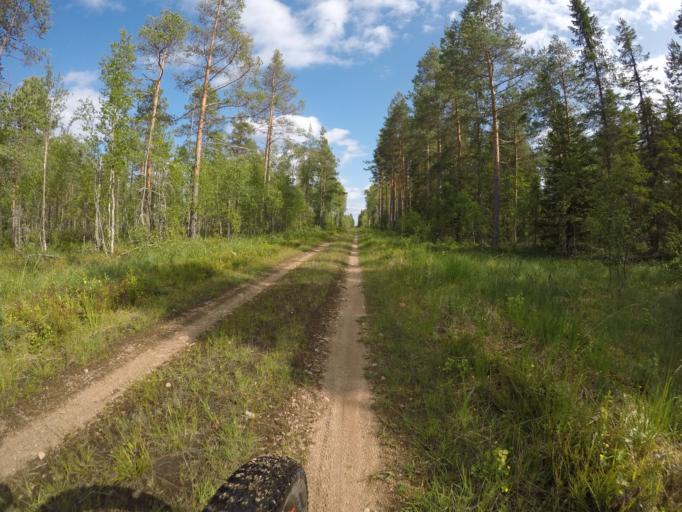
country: SE
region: OErebro
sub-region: Hallefors Kommun
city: Haellefors
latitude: 60.0883
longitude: 14.4925
